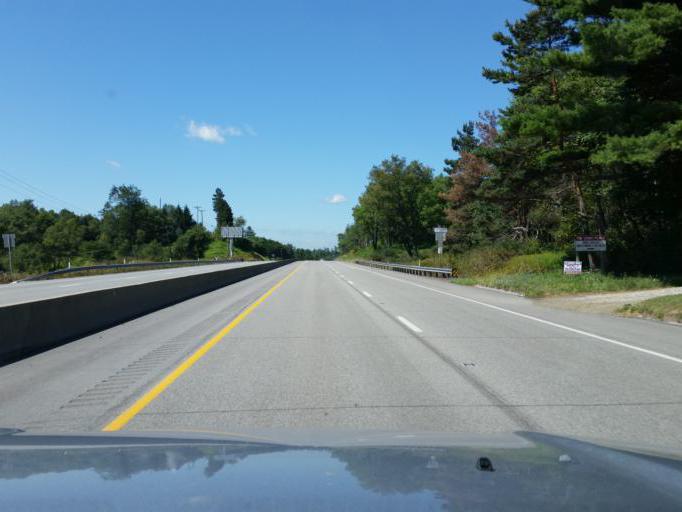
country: US
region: Pennsylvania
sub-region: Cambria County
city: Nanty Glo
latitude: 40.4508
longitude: -78.7880
